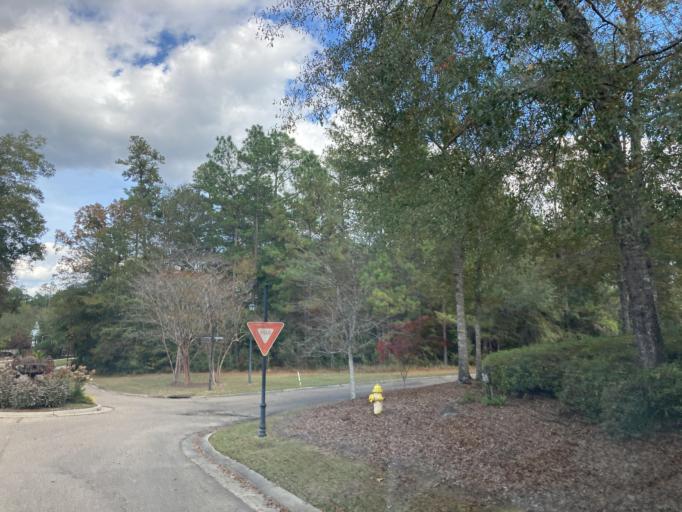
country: US
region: Mississippi
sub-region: Lamar County
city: Arnold Line
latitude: 31.3550
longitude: -89.3790
